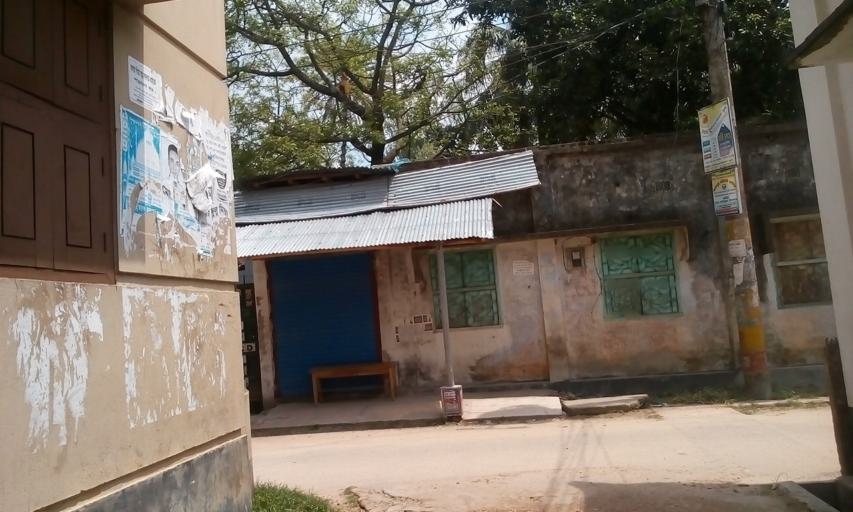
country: IN
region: West Bengal
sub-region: Dakshin Dinajpur
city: Balurghat
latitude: 25.3897
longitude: 88.9883
